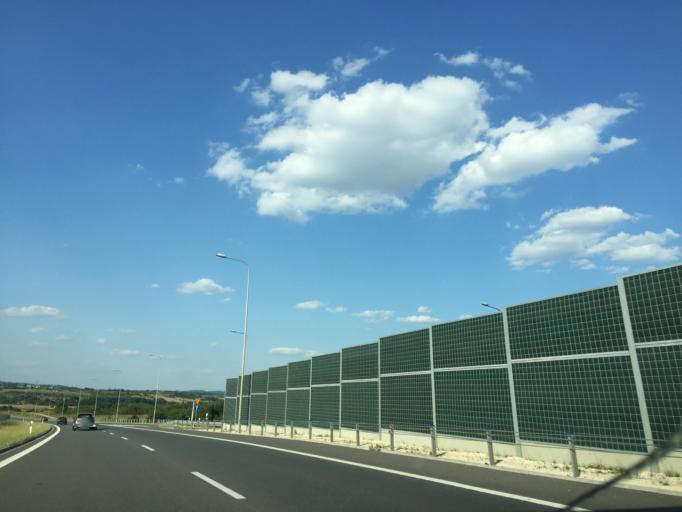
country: PL
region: Swietokrzyskie
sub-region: Powiat kielecki
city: Checiny
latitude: 50.7587
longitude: 20.4608
